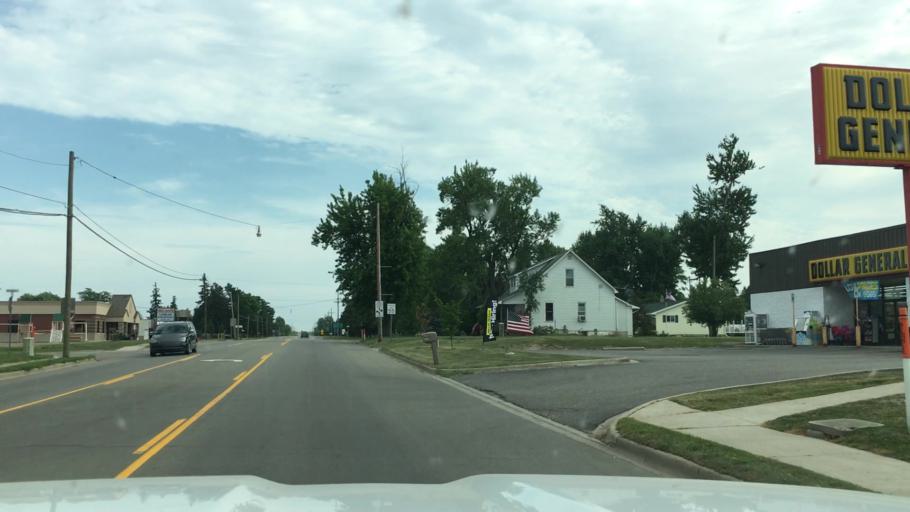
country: US
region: Michigan
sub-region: Sanilac County
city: Marlette
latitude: 43.3174
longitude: -83.0799
